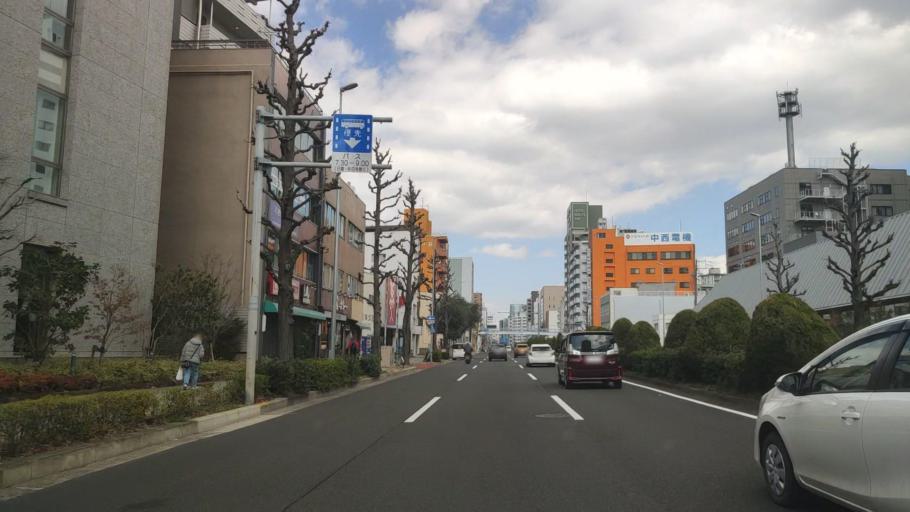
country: JP
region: Aichi
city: Nagoya-shi
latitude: 35.1523
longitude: 136.9048
